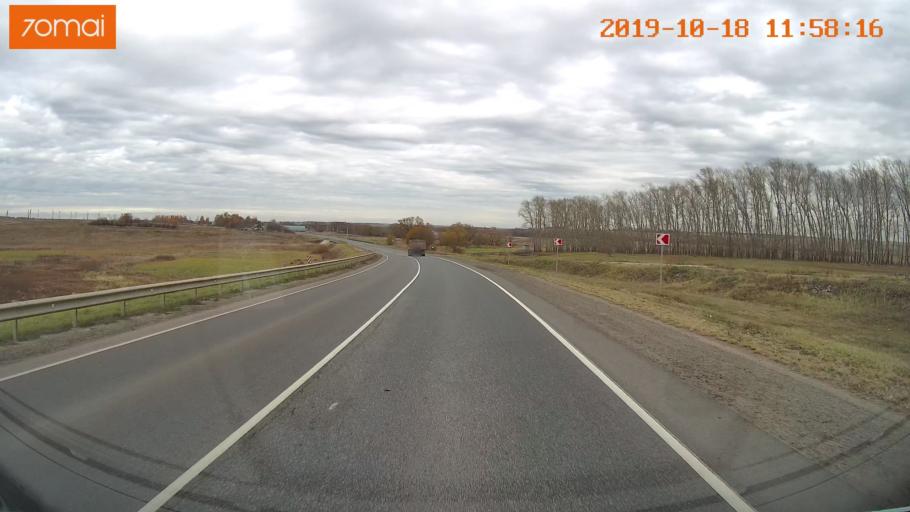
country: RU
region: Rjazan
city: Mikhaylov
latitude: 54.2699
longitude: 39.1650
